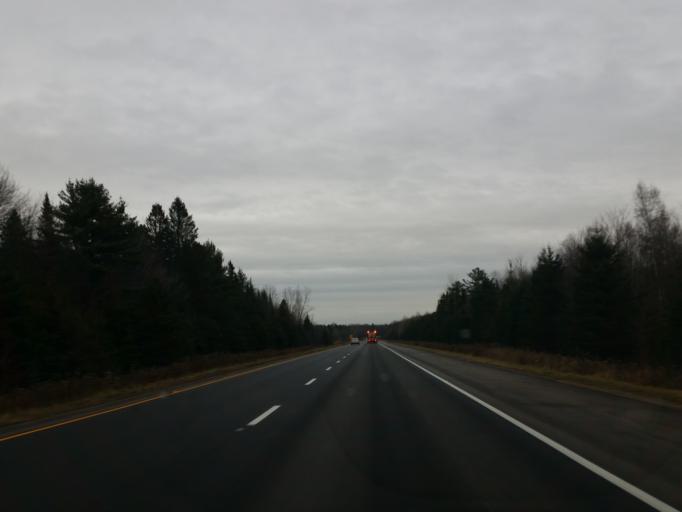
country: CA
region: Quebec
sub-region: Capitale-Nationale
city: Cap-Sante
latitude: 46.7014
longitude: -71.8635
